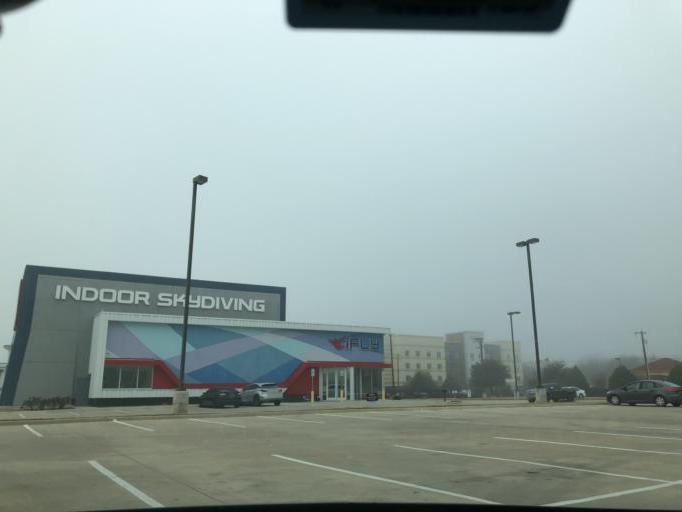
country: US
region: Texas
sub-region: Tarrant County
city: Richland Hills
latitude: 32.8218
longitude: -97.2066
